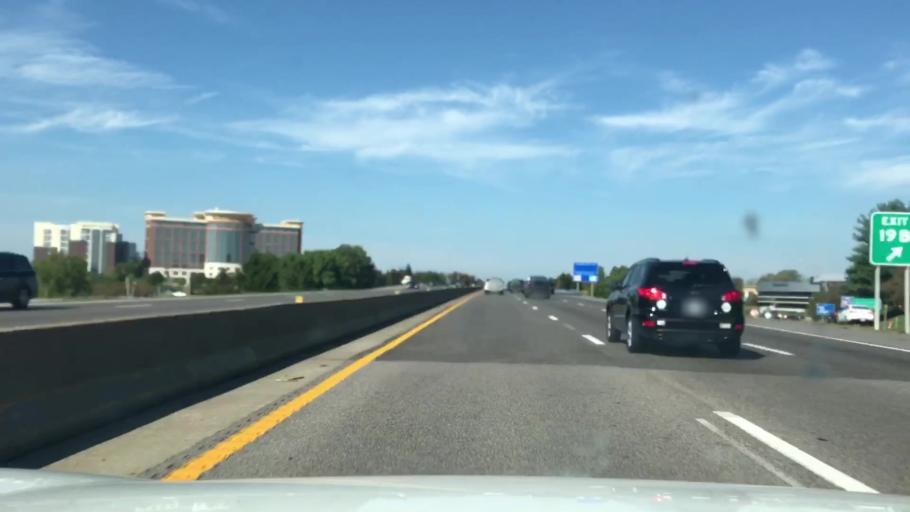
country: US
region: Missouri
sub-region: Saint Louis County
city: Chesterfield
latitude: 38.6523
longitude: -90.5556
